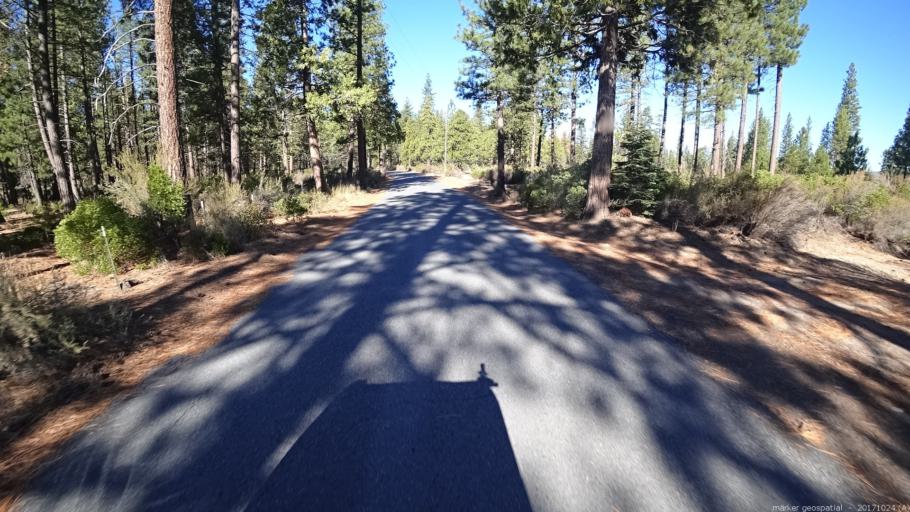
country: US
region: California
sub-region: Shasta County
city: Burney
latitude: 40.7530
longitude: -121.4792
